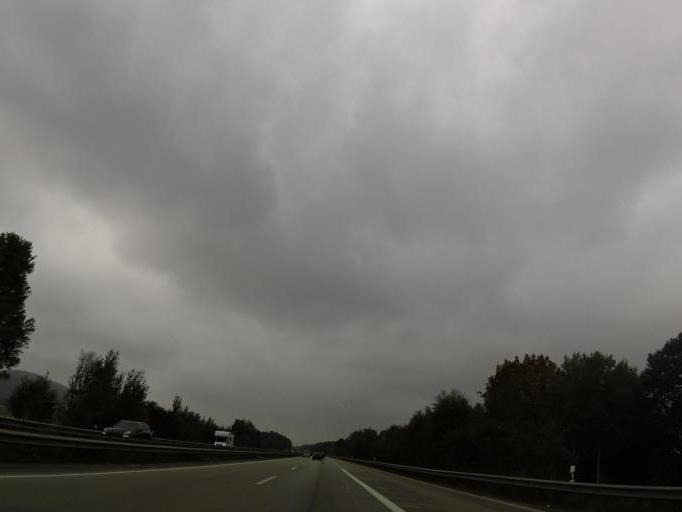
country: DE
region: Rheinland-Pfalz
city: Hauptstuhl
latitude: 49.3973
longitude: 7.4604
